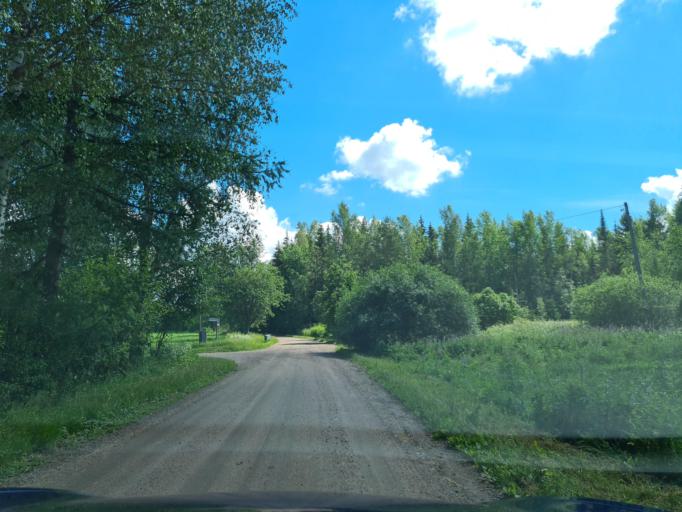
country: FI
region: Uusimaa
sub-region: Helsinki
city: Kaerkoelae
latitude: 60.7552
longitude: 23.9529
